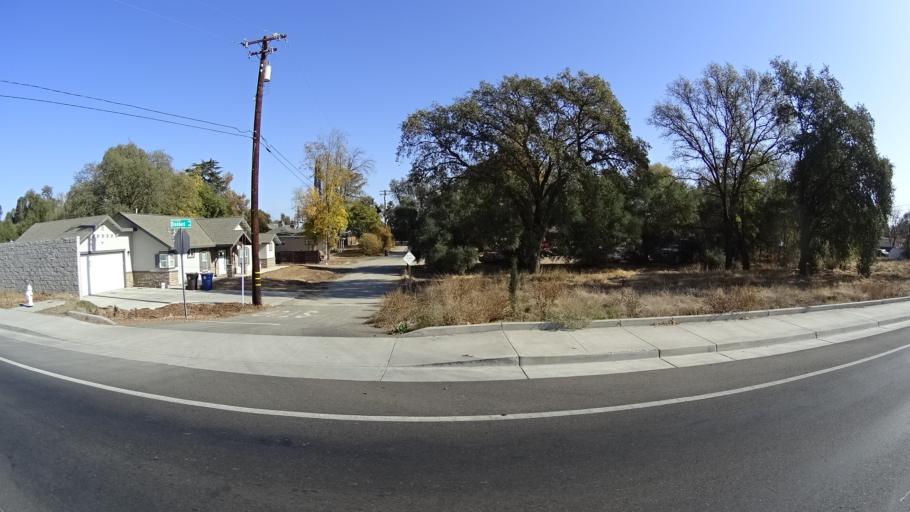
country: US
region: California
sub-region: Sacramento County
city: Citrus Heights
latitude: 38.6812
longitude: -121.2903
